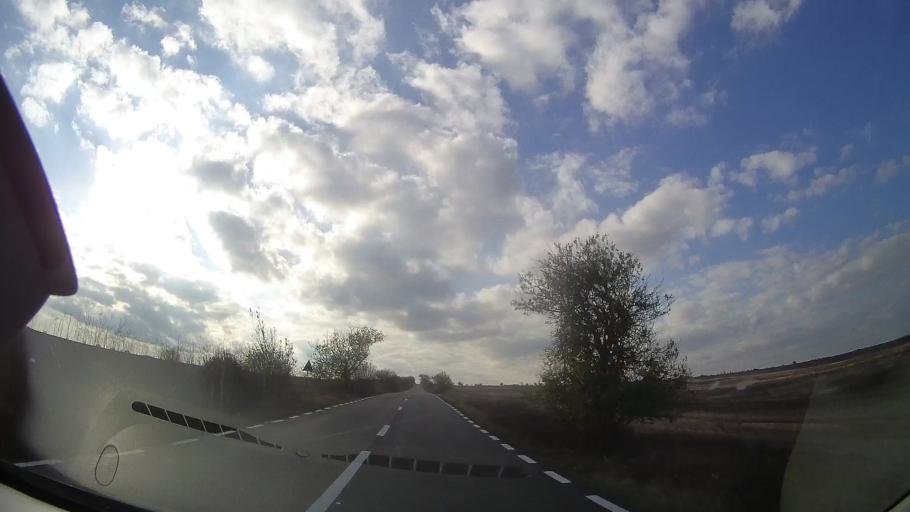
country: RO
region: Constanta
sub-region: Comuna Albesti
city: Albesti
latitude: 43.8148
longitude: 28.4532
